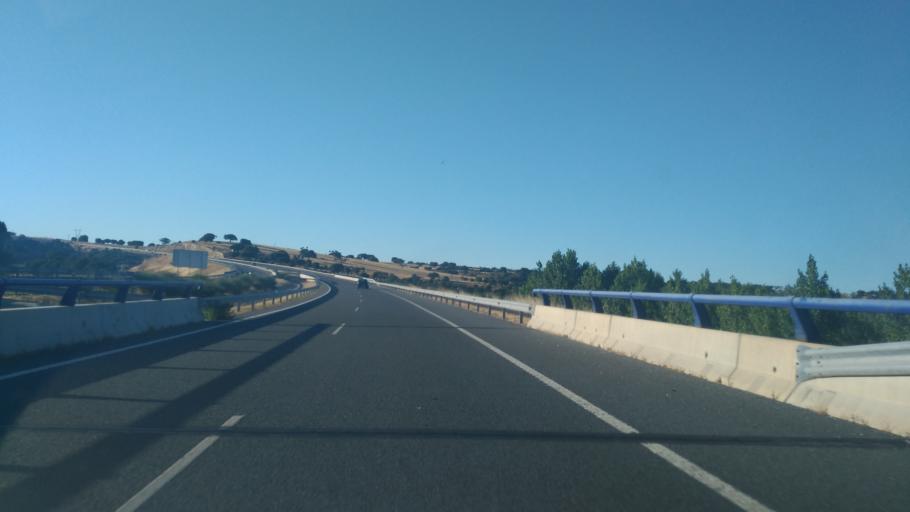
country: ES
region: Castille and Leon
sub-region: Provincia de Salamanca
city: Belena
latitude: 40.7126
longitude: -5.6232
